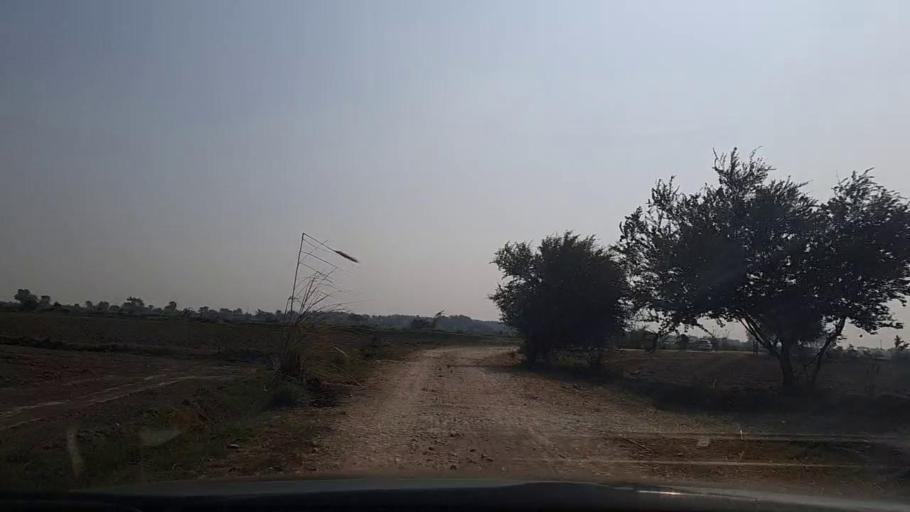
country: PK
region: Sindh
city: Mirpur Sakro
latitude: 24.5661
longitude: 67.7775
